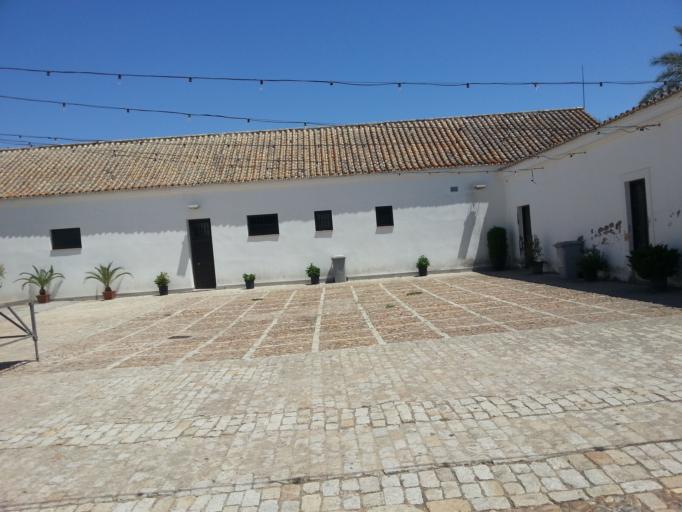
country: ES
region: Andalusia
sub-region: Provincia de Sevilla
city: Camas
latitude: 37.4214
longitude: -5.9959
